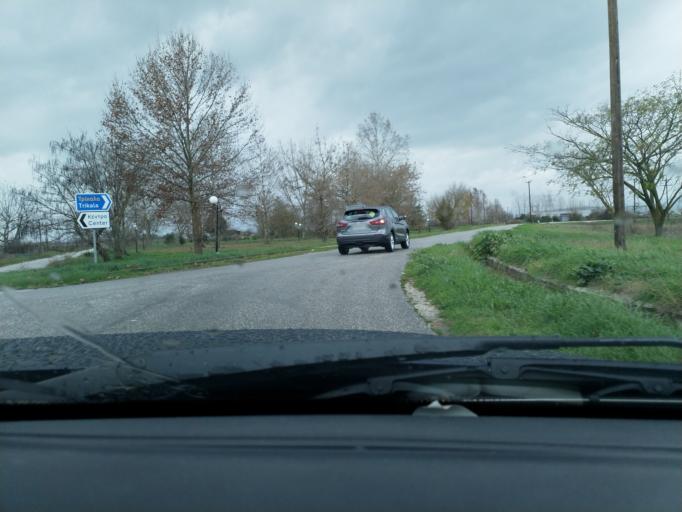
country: GR
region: Thessaly
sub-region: Trikala
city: Taxiarches
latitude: 39.5505
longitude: 21.8914
